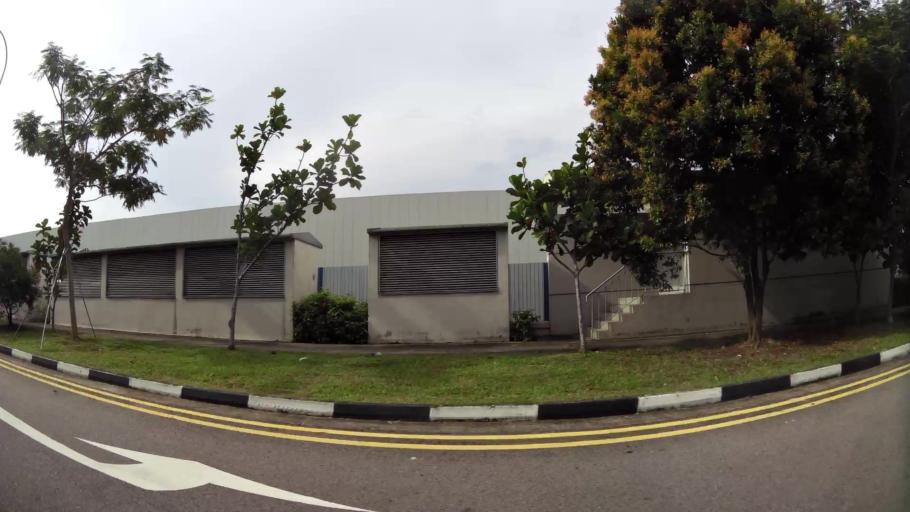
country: SG
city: Singapore
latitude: 1.3432
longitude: 103.8907
